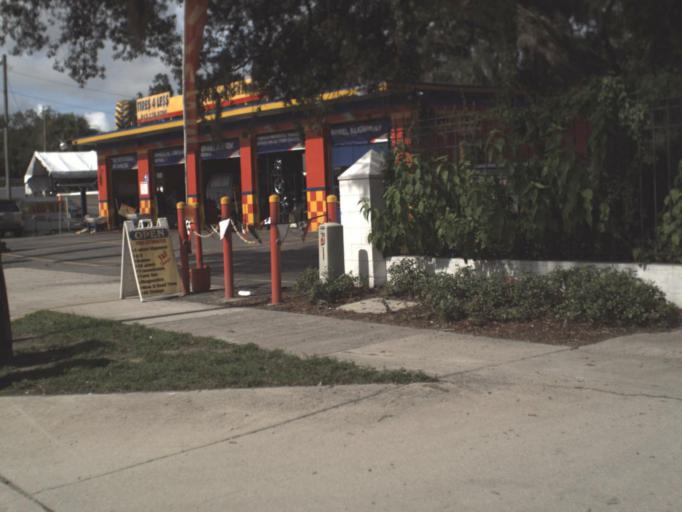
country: US
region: Florida
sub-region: Hillsborough County
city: Egypt Lake-Leto
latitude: 28.0052
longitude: -82.4514
